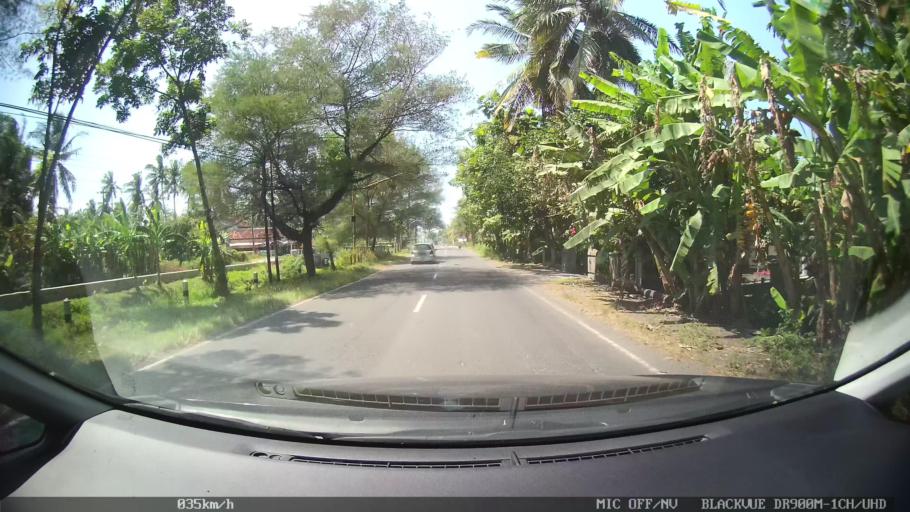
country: ID
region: Daerah Istimewa Yogyakarta
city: Srandakan
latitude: -7.9377
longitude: 110.1545
